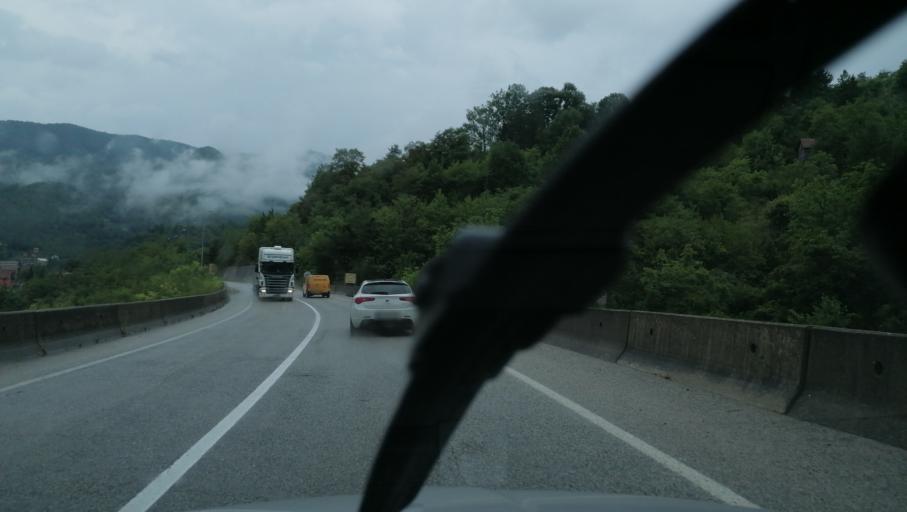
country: BA
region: Republika Srpska
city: Visegrad
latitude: 43.7334
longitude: 19.1828
